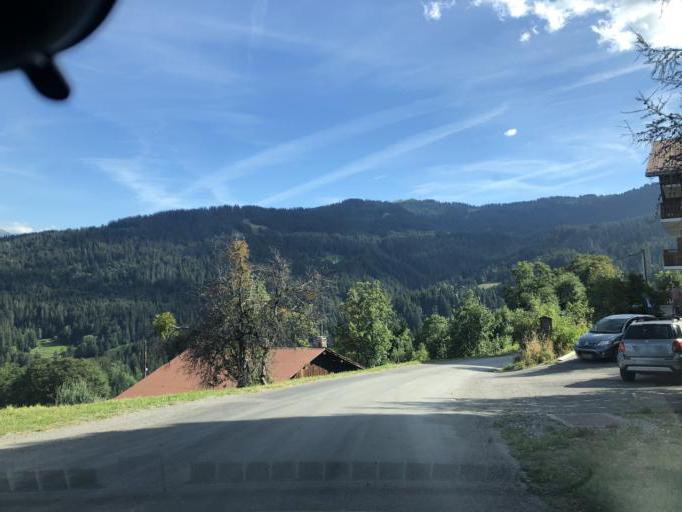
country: FR
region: Rhone-Alpes
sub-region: Departement de la Haute-Savoie
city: Cordon
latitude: 45.9117
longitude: 6.5912
